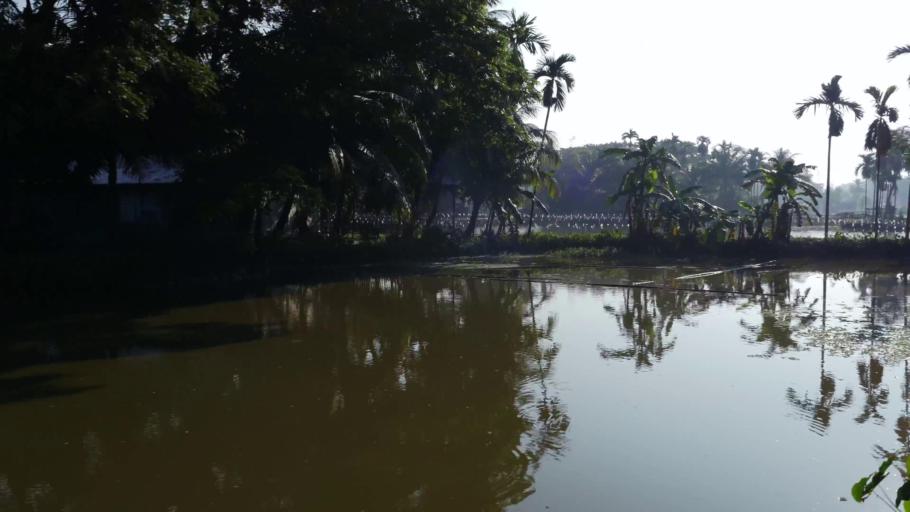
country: BD
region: Dhaka
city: Jamalpur
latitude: 24.8653
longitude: 90.0501
